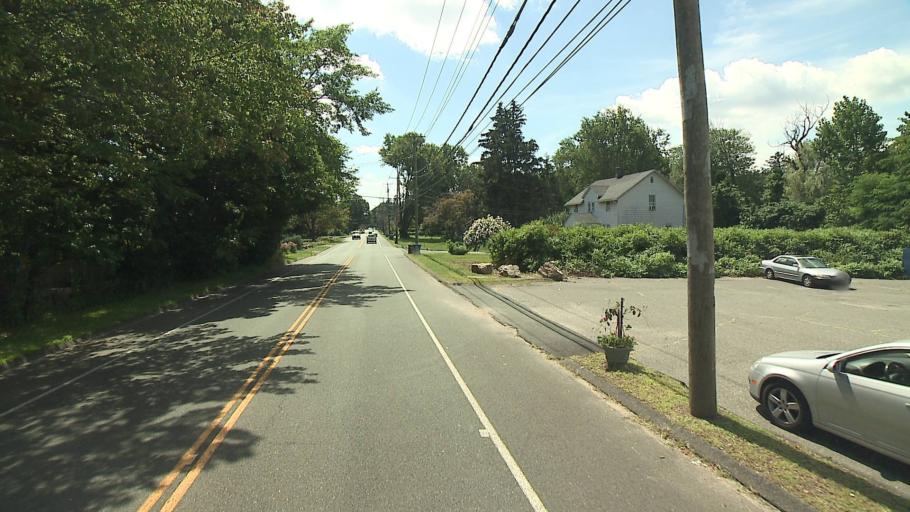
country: US
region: Connecticut
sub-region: Fairfield County
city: Trumbull
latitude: 41.2496
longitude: -73.2204
